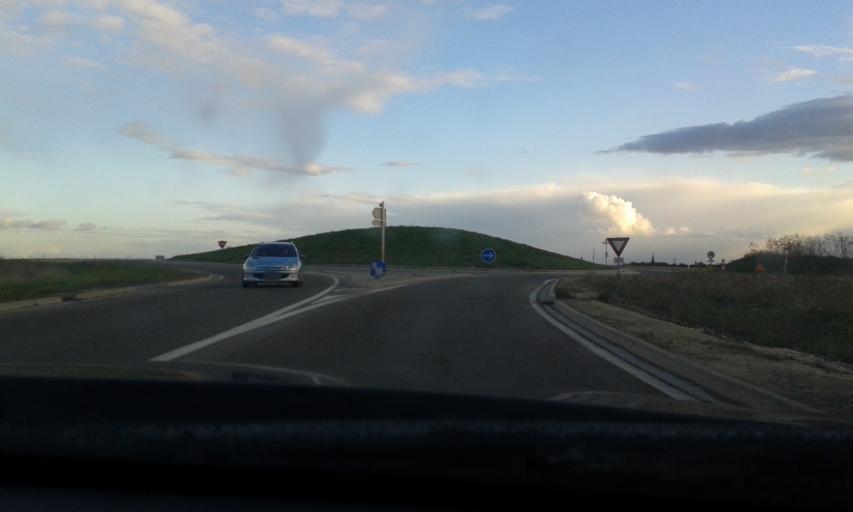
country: FR
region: Centre
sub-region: Departement d'Eure-et-Loir
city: Voves
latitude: 48.2747
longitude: 1.7398
